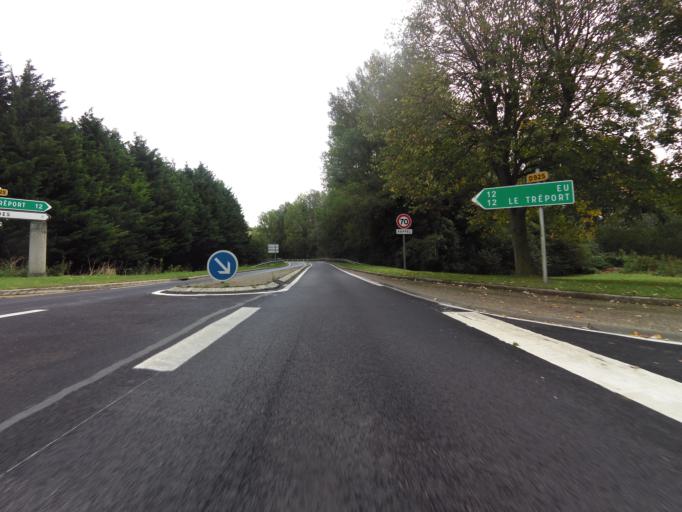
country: FR
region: Haute-Normandie
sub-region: Departement de la Seine-Maritime
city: Criel-sur-Mer
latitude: 50.0102
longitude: 1.3176
